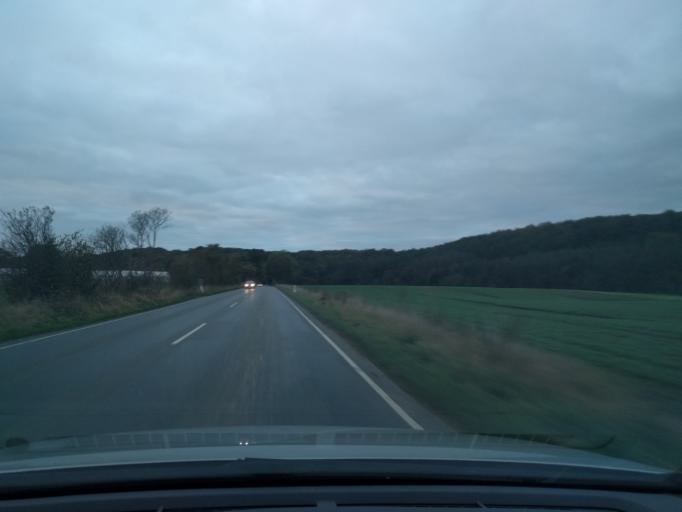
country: DK
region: South Denmark
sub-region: Odense Kommune
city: Bellinge
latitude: 55.2206
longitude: 10.2980
